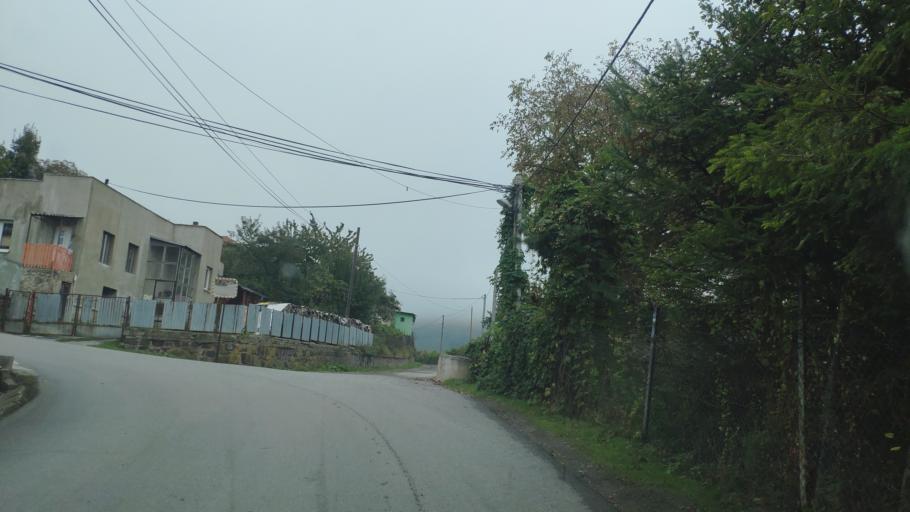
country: SK
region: Presovsky
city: Vranov nad Topl'ou
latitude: 48.8793
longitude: 21.4493
